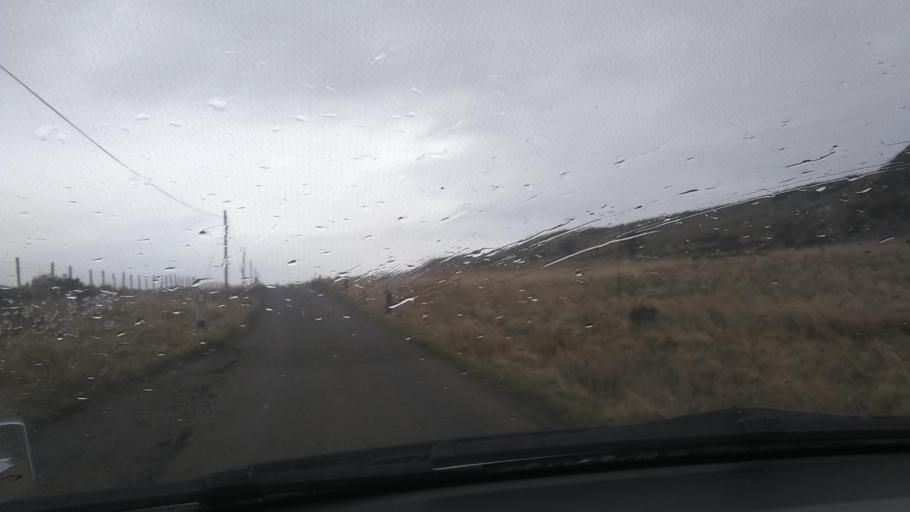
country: GB
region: England
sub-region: Worcestershire
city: Tenbury Wells
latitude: 52.3858
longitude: -2.6019
